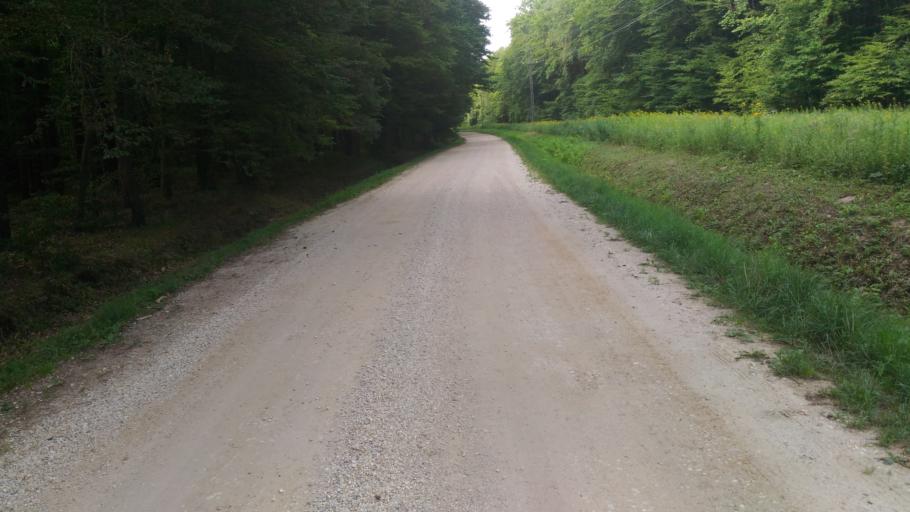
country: HU
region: Zala
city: Zalalovo
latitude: 46.8114
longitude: 16.5312
